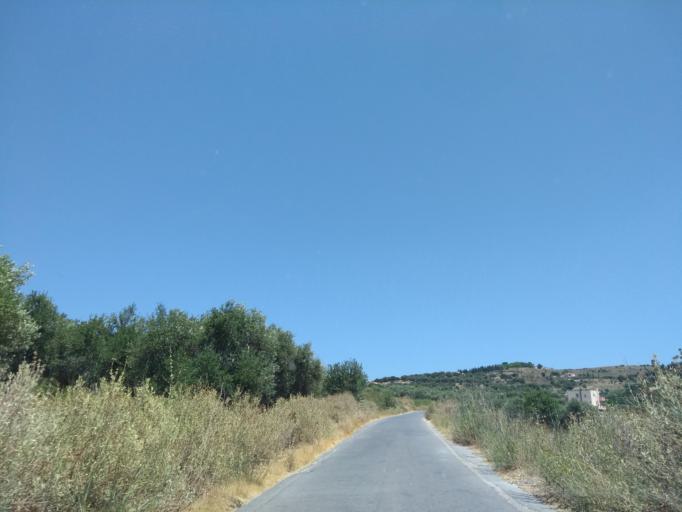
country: GR
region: Crete
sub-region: Nomos Chanias
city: Georgioupolis
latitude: 35.3257
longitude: 24.3250
